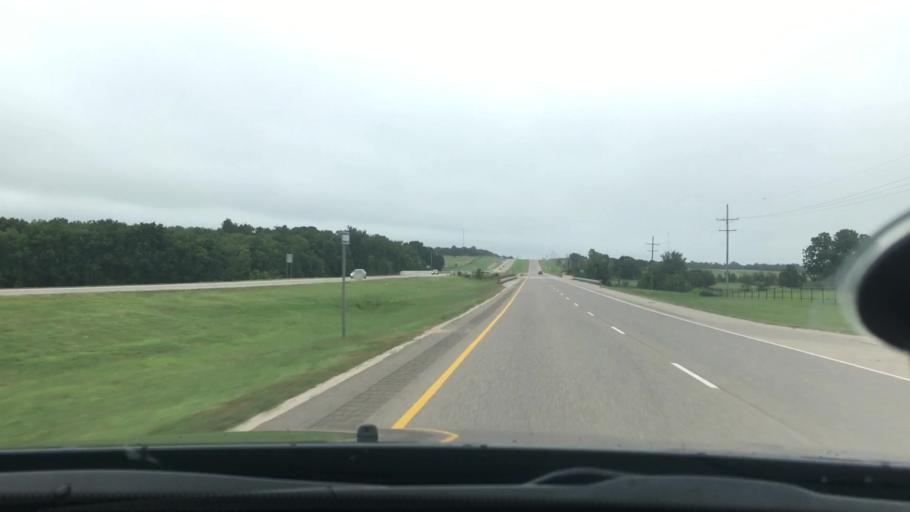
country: US
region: Oklahoma
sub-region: Lincoln County
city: Prague
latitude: 35.3578
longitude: -96.6715
